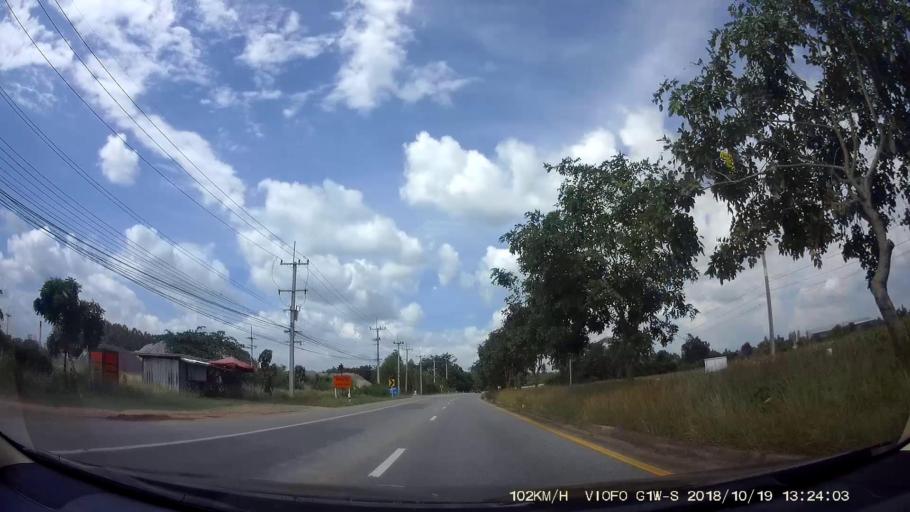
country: TH
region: Chaiyaphum
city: Chatturat
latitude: 15.5017
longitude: 101.8201
